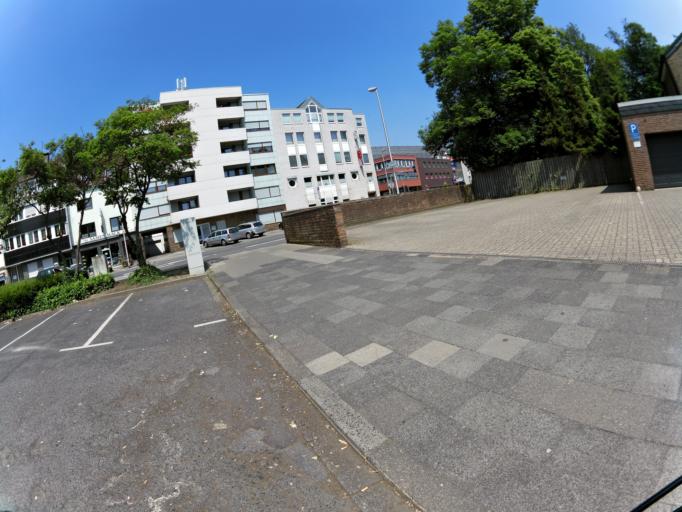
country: DE
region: North Rhine-Westphalia
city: Julich
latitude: 50.9208
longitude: 6.3609
